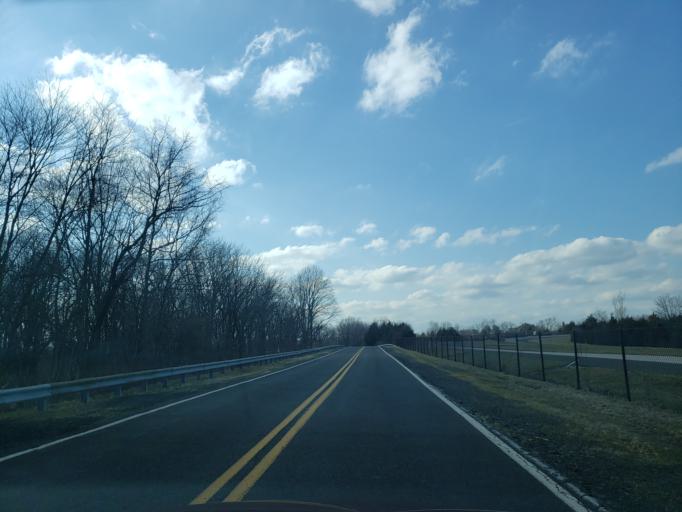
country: US
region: Pennsylvania
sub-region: Bucks County
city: Doylestown
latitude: 40.2913
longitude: -75.1366
